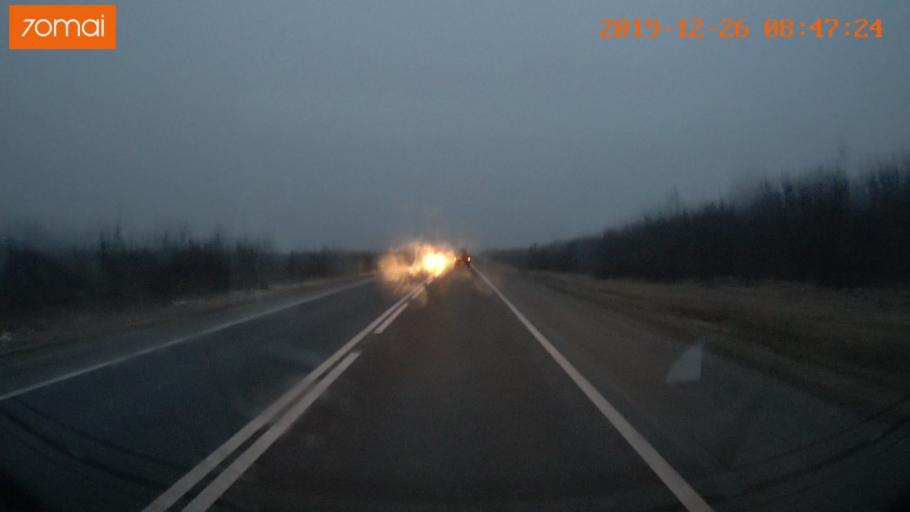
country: RU
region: Jaroslavl
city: Prechistoye
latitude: 58.6225
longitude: 40.3317
